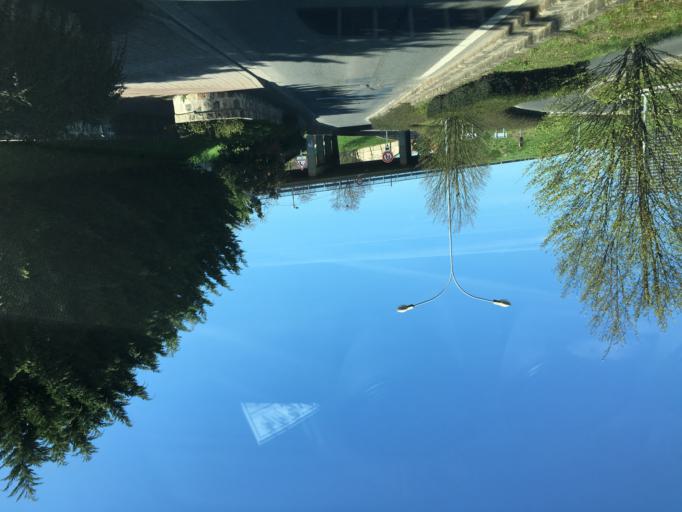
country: FR
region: Ile-de-France
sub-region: Departement de l'Essonne
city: Montgeron
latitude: 48.7071
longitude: 2.4417
